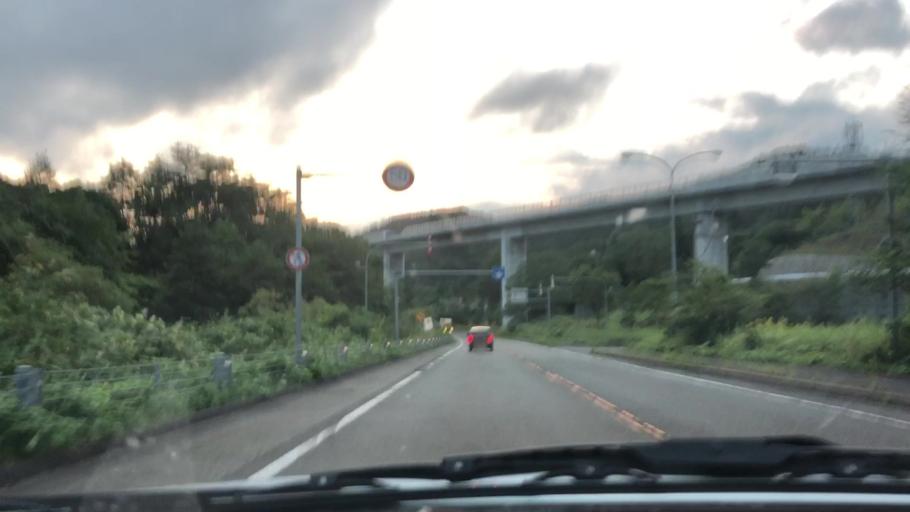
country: JP
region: Hokkaido
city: Iwamizawa
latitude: 42.9333
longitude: 142.0840
